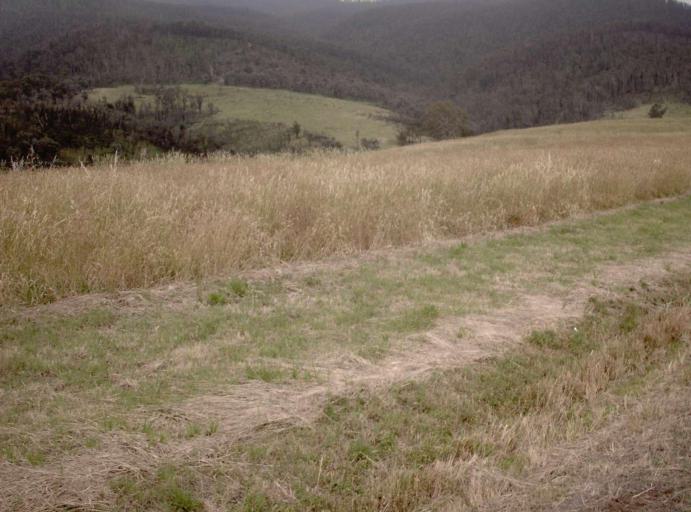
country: AU
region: Victoria
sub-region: Wellington
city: Heyfield
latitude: -37.8351
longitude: 146.6816
